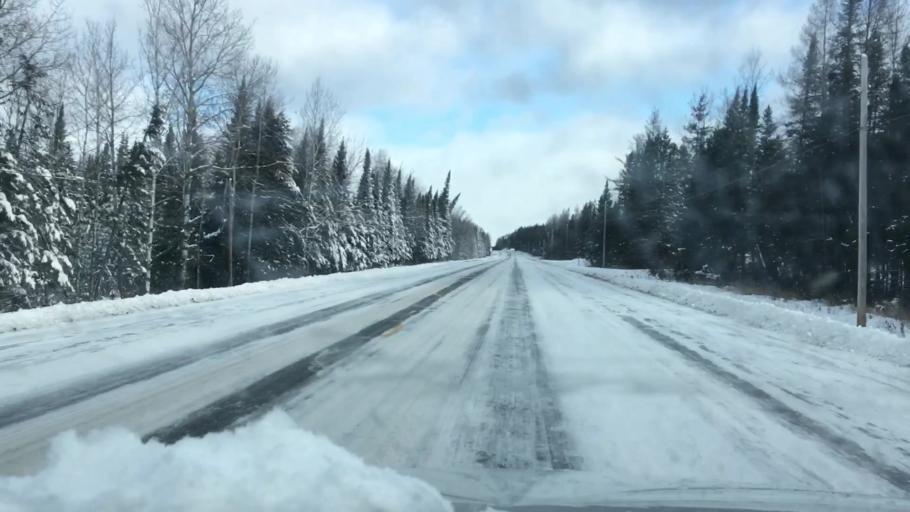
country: US
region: Maine
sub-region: Aroostook County
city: Van Buren
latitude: 47.0292
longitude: -68.0090
